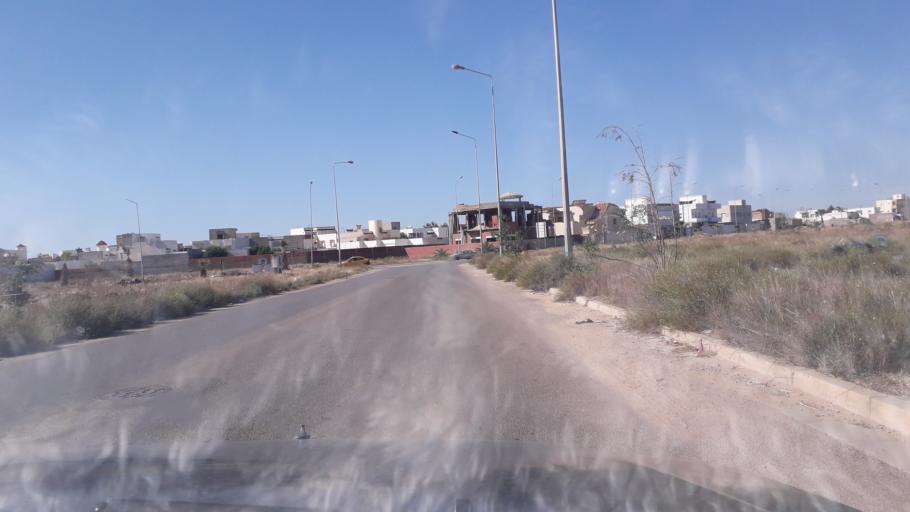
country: TN
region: Safaqis
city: Al Qarmadah
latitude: 34.8290
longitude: 10.7535
